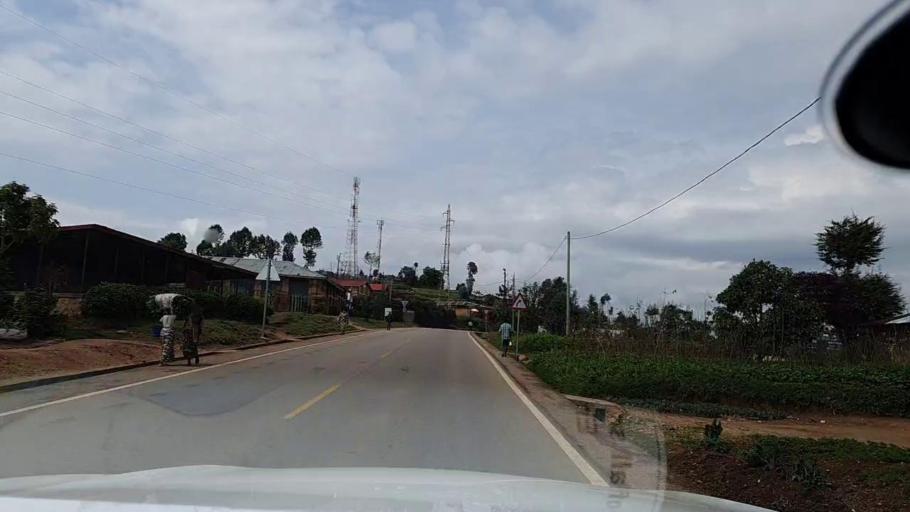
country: RW
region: Southern Province
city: Nzega
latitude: -2.4838
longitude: 29.5323
